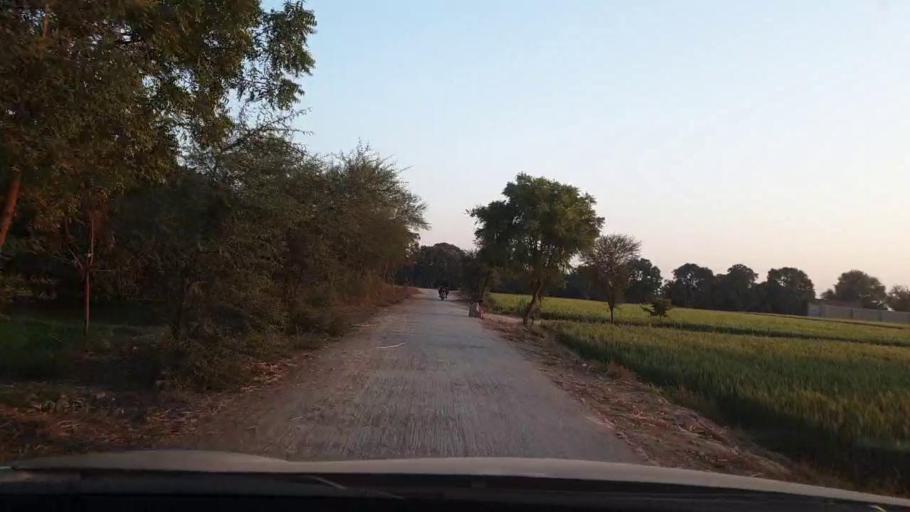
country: PK
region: Sindh
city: Tando Allahyar
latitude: 25.5241
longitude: 68.7447
